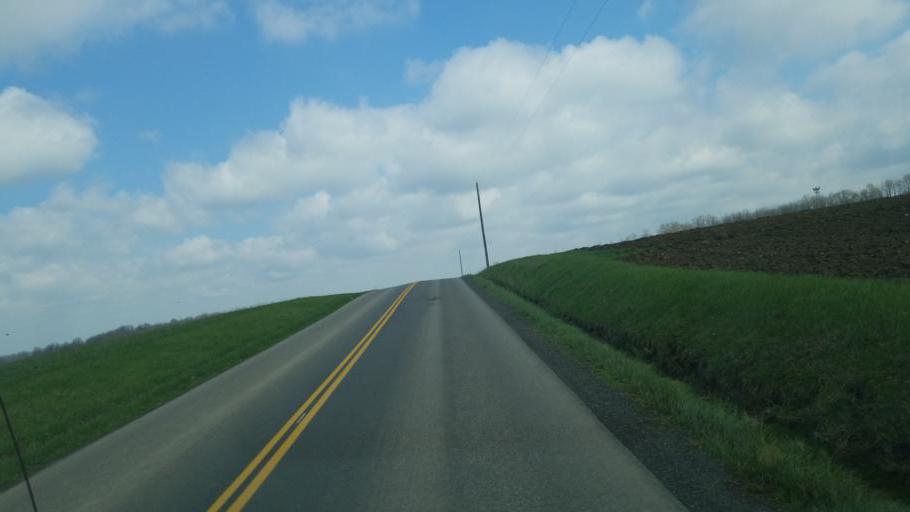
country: US
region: Ohio
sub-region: Wayne County
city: Apple Creek
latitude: 40.6422
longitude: -81.8467
